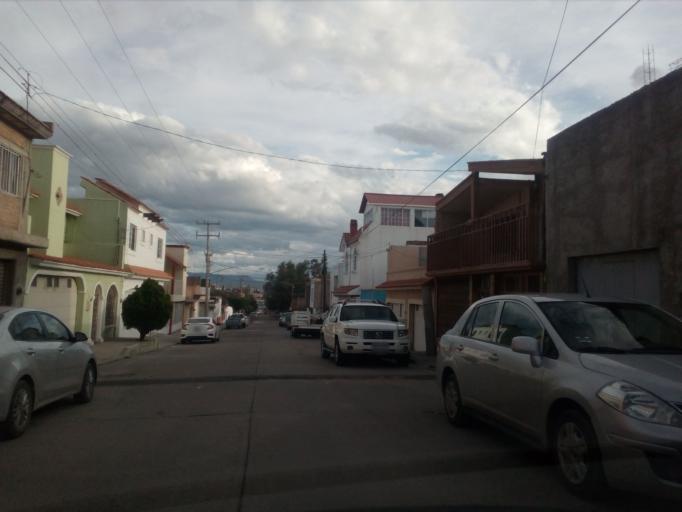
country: MX
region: Durango
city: Victoria de Durango
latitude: 24.0425
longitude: -104.6657
